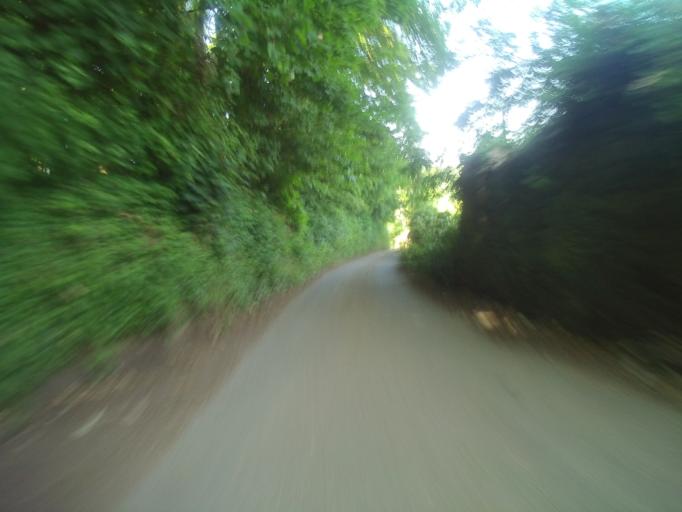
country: GB
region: England
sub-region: Devon
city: Dartmouth
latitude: 50.3543
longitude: -3.5979
